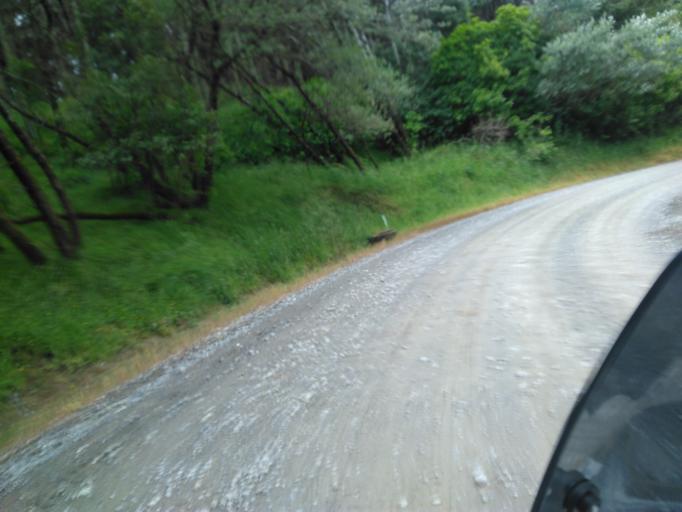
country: NZ
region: Gisborne
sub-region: Gisborne District
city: Gisborne
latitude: -38.0590
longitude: 178.1540
